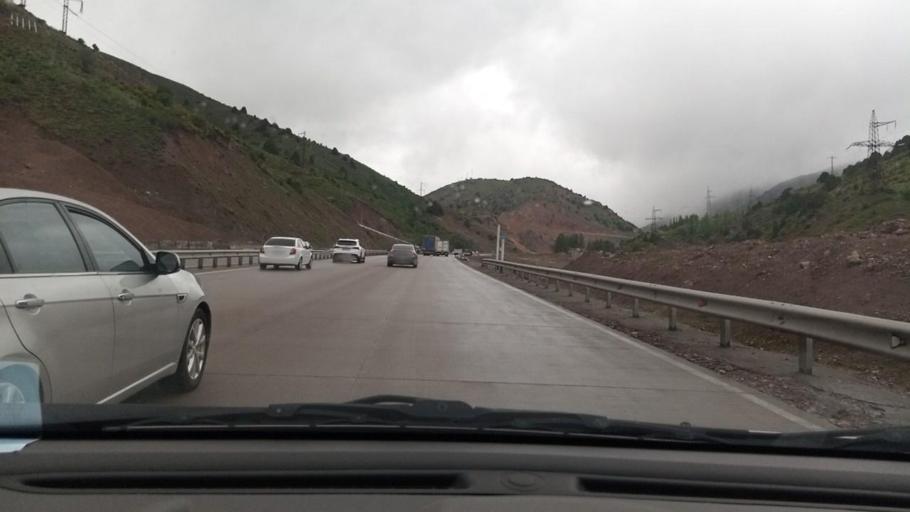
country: UZ
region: Toshkent
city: Angren
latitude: 41.0594
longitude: 70.5616
